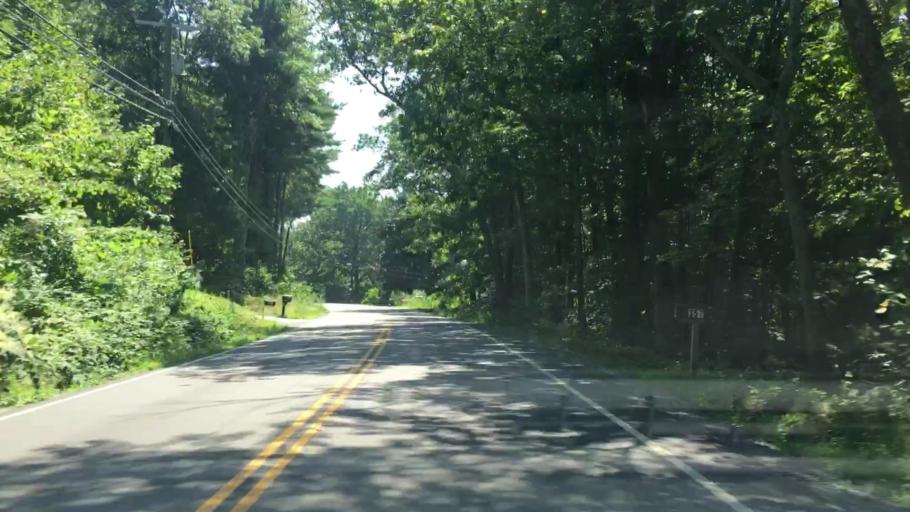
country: US
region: New Hampshire
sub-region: Rockingham County
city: Hampstead
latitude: 42.8624
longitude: -71.2238
